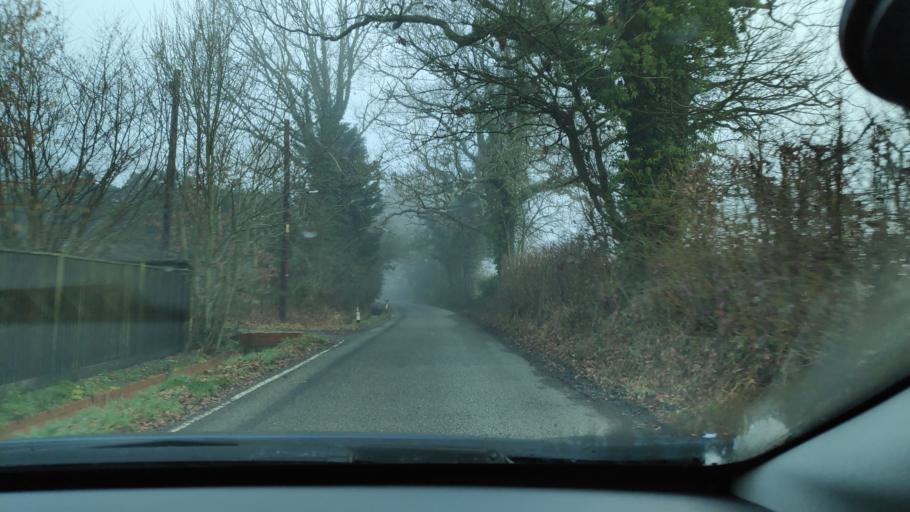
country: GB
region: England
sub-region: Surrey
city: Seale
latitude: 51.2476
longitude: -0.7050
